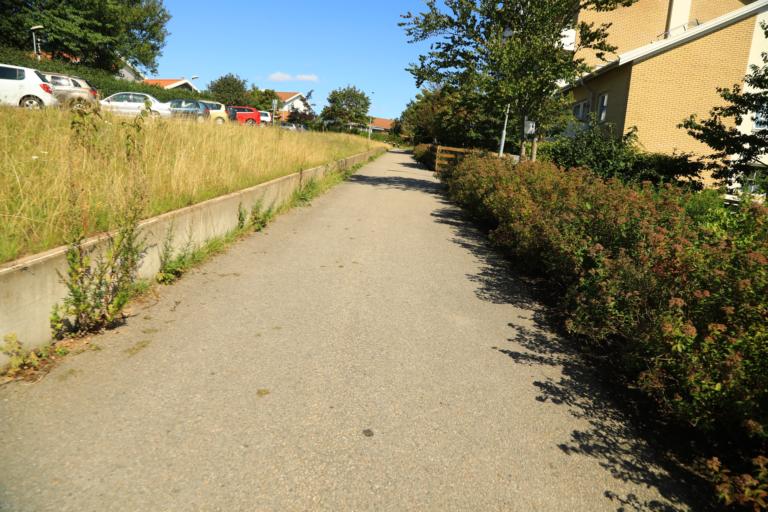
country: SE
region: Halland
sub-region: Varbergs Kommun
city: Varberg
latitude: 57.0911
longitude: 12.2688
